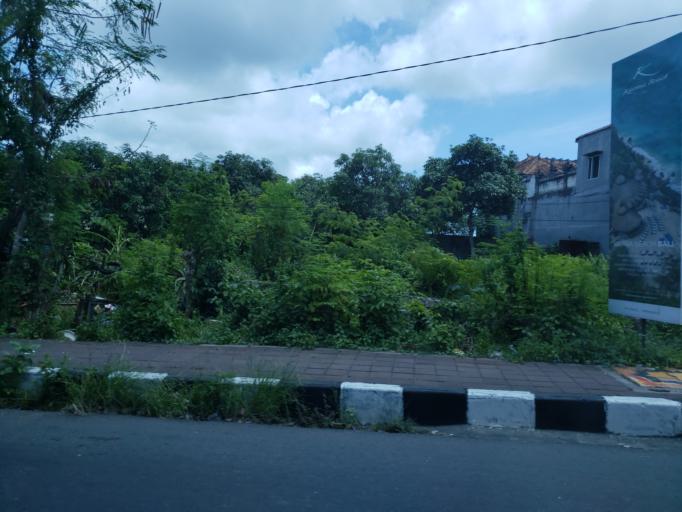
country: ID
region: Bali
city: Jimbaran
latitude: -8.8137
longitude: 115.1571
